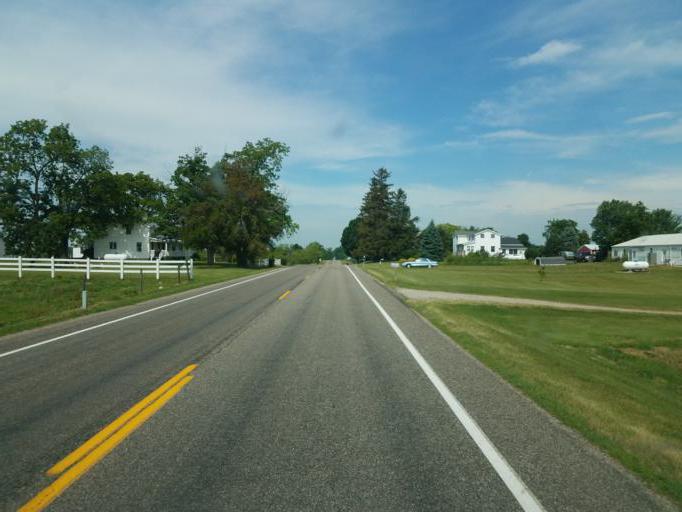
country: US
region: Michigan
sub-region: Eaton County
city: Charlotte
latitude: 42.6263
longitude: -84.9217
